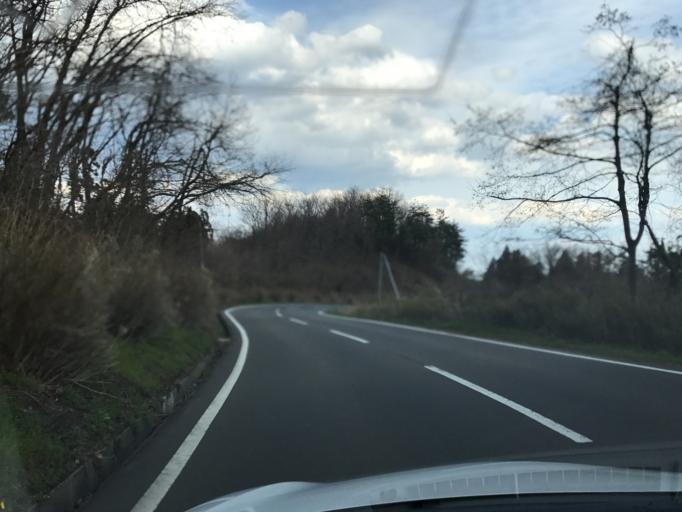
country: JP
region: Miyagi
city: Shiroishi
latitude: 38.0195
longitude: 140.5716
